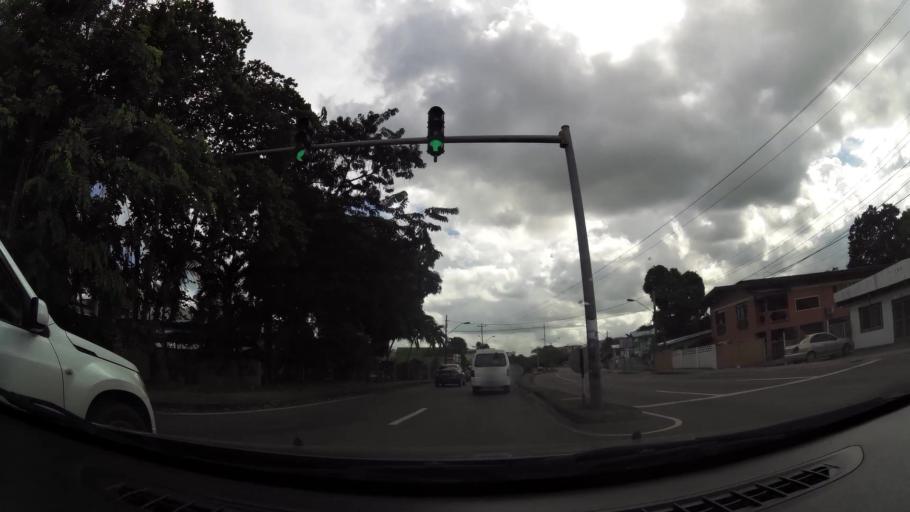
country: TT
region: City of San Fernando
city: San Fernando
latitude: 10.2714
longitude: -61.4683
